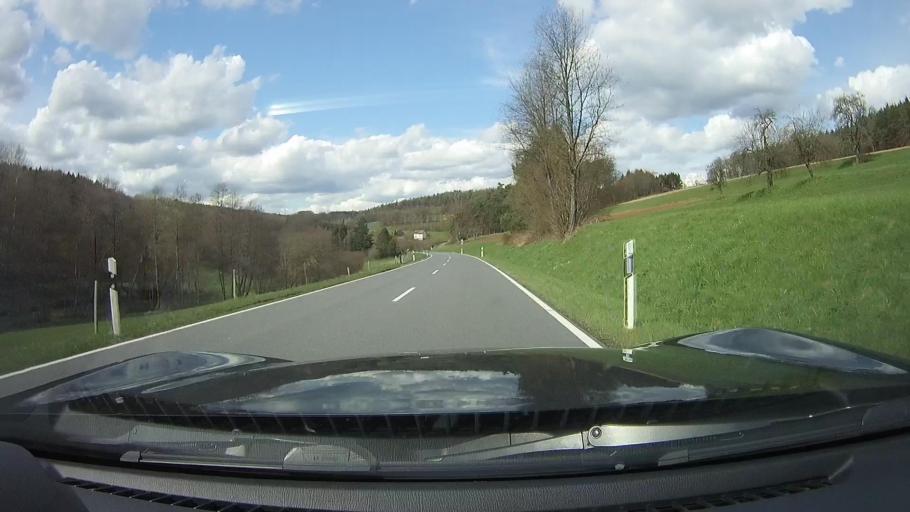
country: DE
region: Baden-Wuerttemberg
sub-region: Karlsruhe Region
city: Mudau
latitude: 49.5505
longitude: 9.2084
